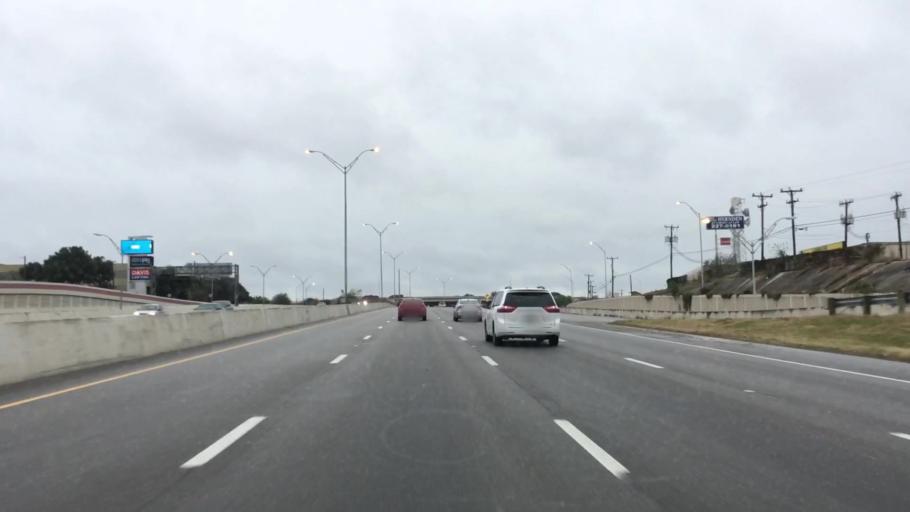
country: US
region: Texas
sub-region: Bexar County
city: Castle Hills
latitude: 29.5345
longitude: -98.4893
